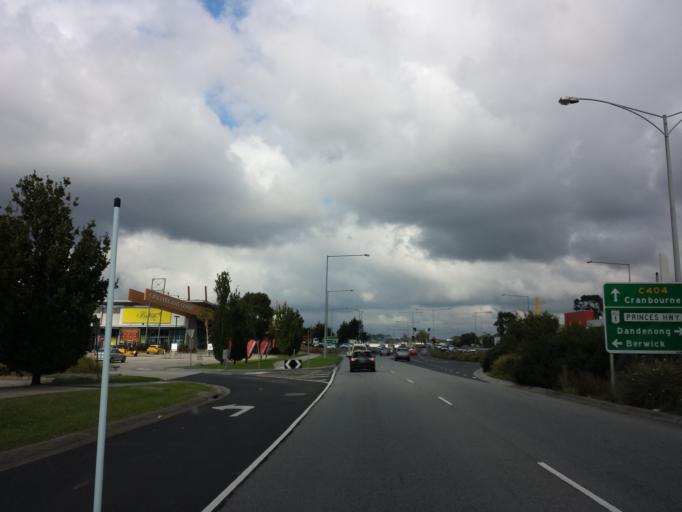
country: AU
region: Victoria
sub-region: Casey
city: Narre Warren
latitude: -38.0244
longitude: 145.3073
